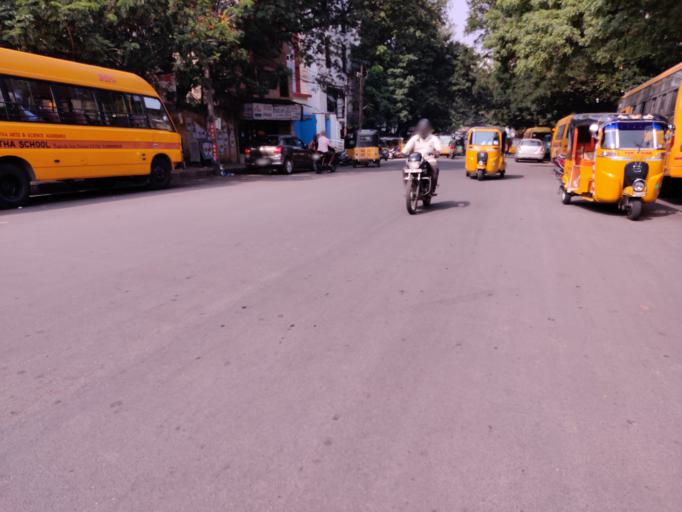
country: IN
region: Telangana
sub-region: Hyderabad
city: Hyderabad
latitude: 17.3956
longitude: 78.4730
